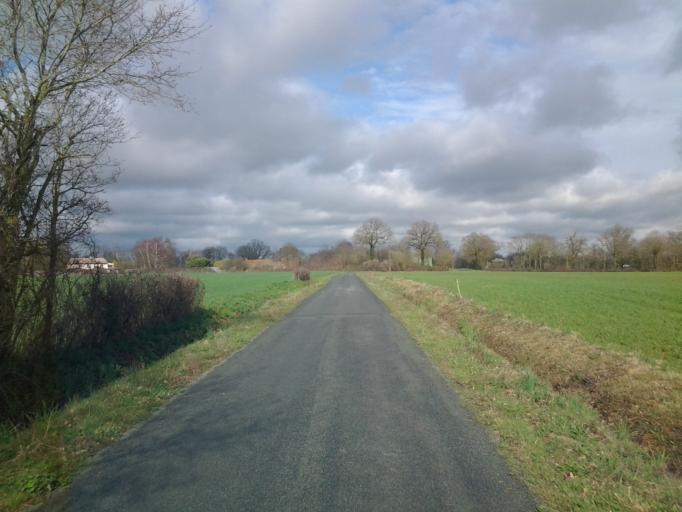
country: FR
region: Pays de la Loire
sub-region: Departement de la Vendee
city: La Chaize-le-Vicomte
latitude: 46.6556
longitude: -1.3542
